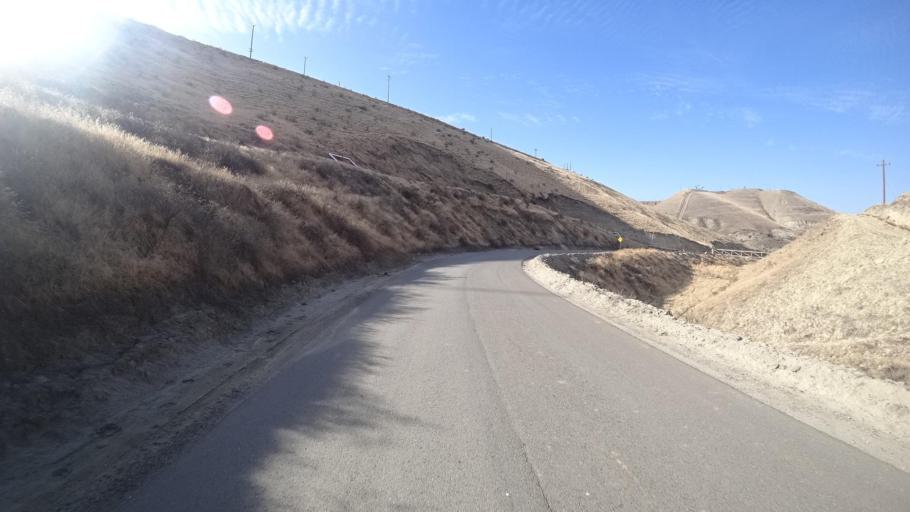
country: US
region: California
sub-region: Kern County
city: Oildale
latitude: 35.4984
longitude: -118.8985
